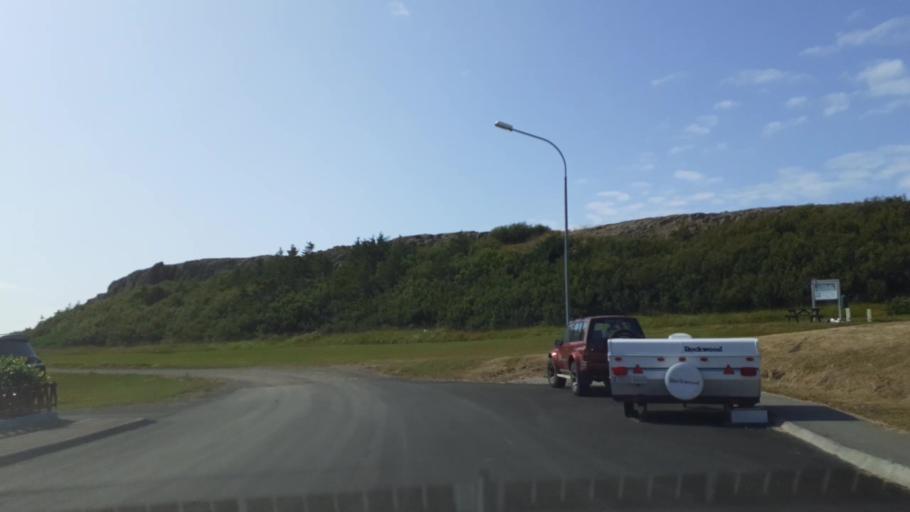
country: IS
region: Northwest
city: Saudarkrokur
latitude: 65.8287
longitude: -20.3204
